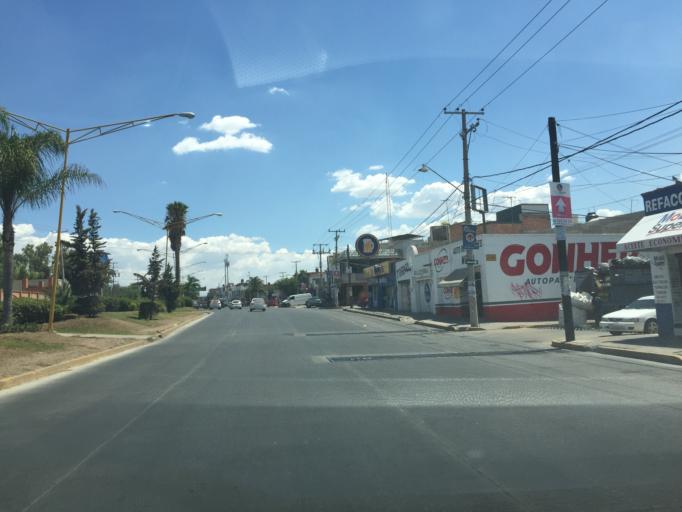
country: MX
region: Aguascalientes
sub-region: Aguascalientes
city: La Loma de los Negritos
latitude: 21.8558
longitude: -102.3163
